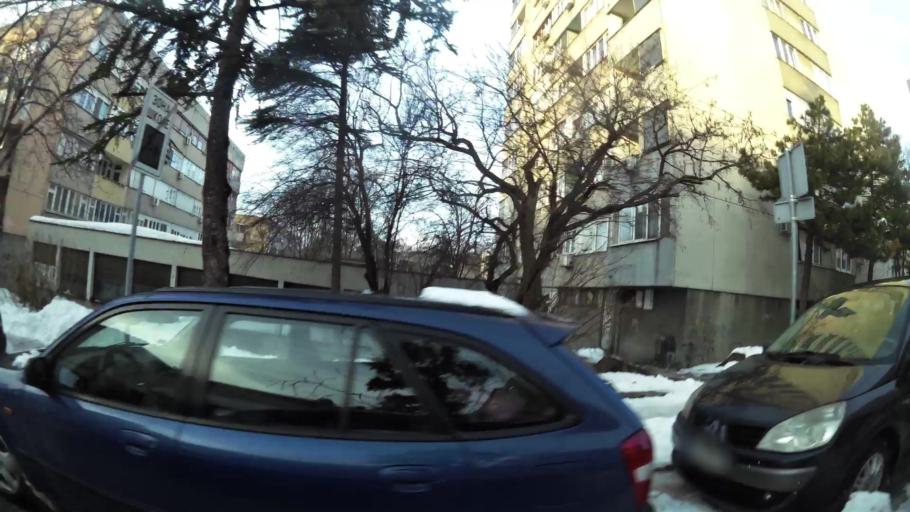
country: RS
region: Central Serbia
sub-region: Belgrade
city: Palilula
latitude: 44.7978
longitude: 20.5027
